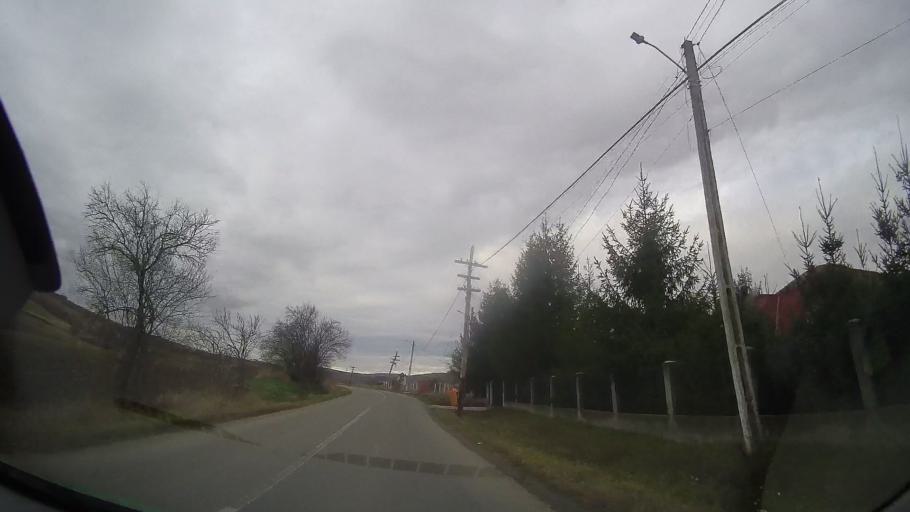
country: RO
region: Mures
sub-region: Comuna Faragau
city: Faragau
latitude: 46.7386
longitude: 24.5404
